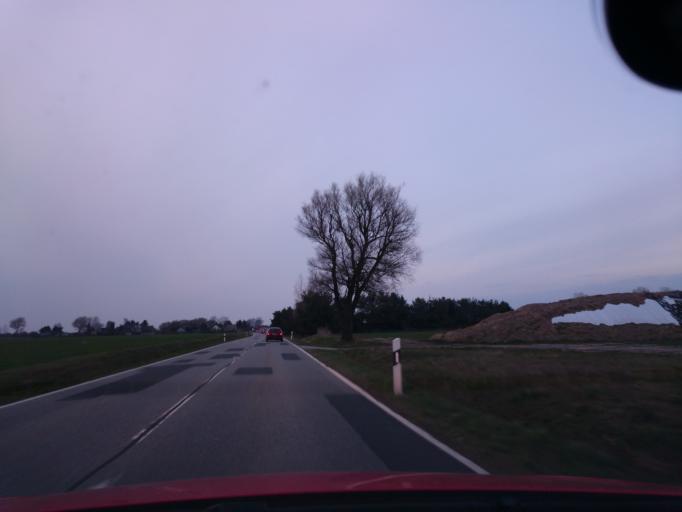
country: DE
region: Mecklenburg-Vorpommern
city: Zingst
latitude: 54.3973
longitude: 12.6774
